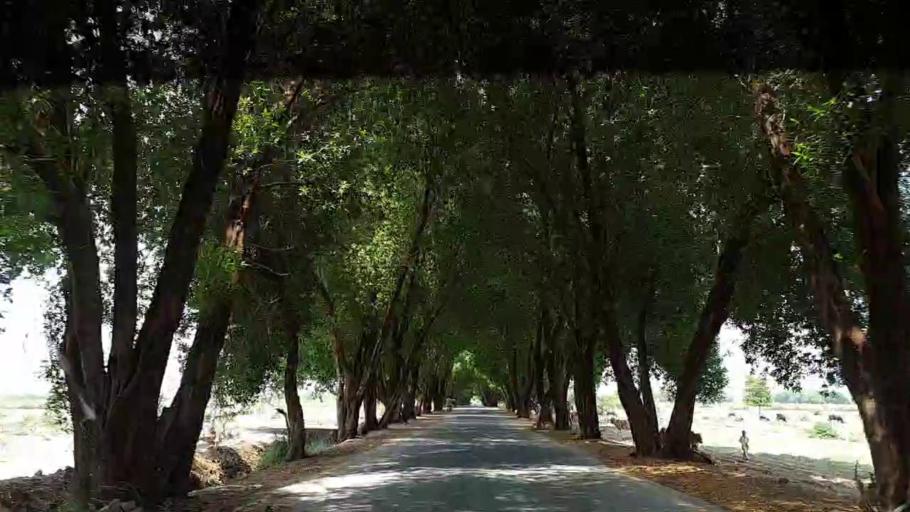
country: PK
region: Sindh
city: Adilpur
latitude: 27.8759
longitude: 69.2741
